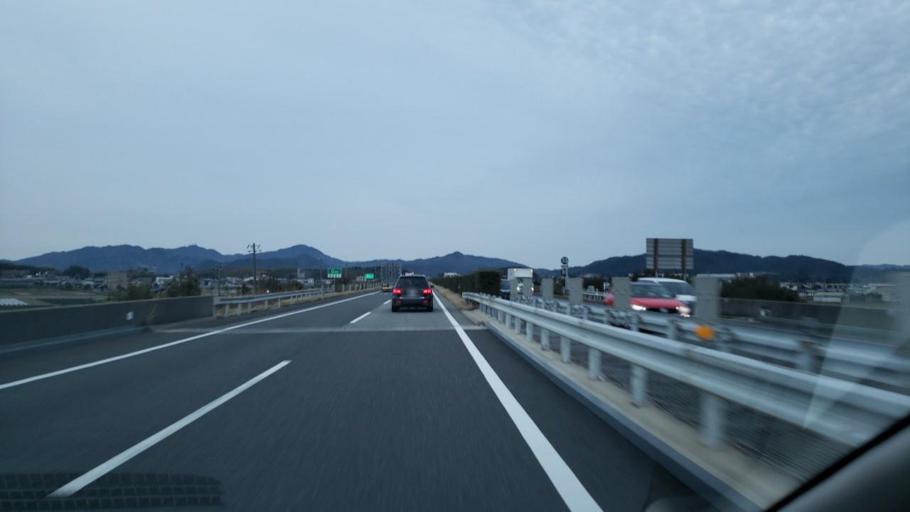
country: JP
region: Hyogo
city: Fukura
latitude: 34.3162
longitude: 134.7619
